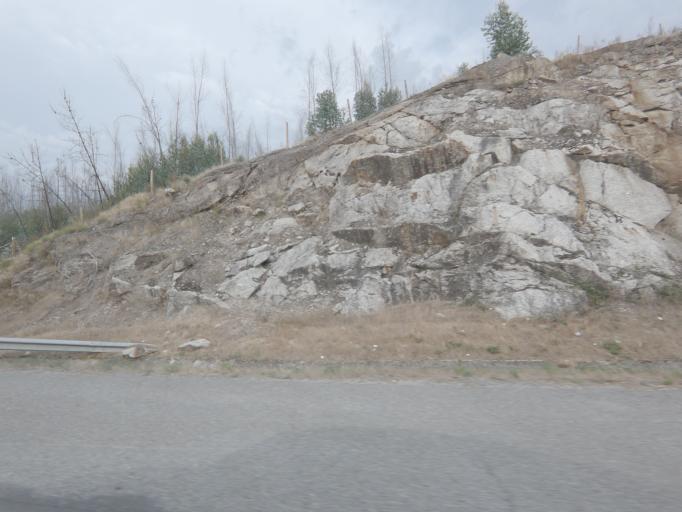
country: PT
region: Viseu
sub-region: Santa Comba Dao
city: Santa Comba Dao
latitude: 40.4485
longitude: -8.1060
